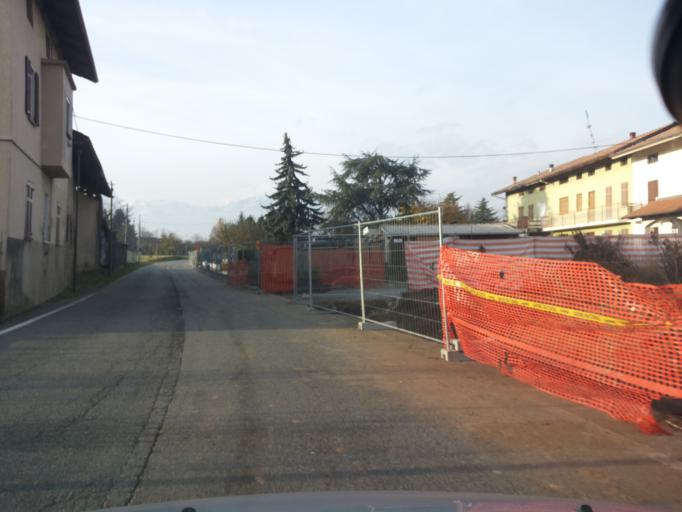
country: IT
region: Piedmont
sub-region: Provincia di Biella
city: Verrone
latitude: 45.5029
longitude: 8.1162
